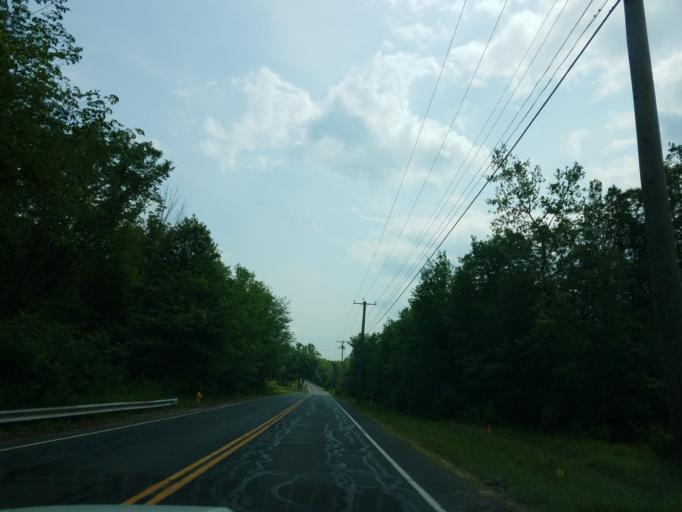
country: US
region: Massachusetts
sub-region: Hampden County
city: Agawam
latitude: 42.0370
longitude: -72.6366
